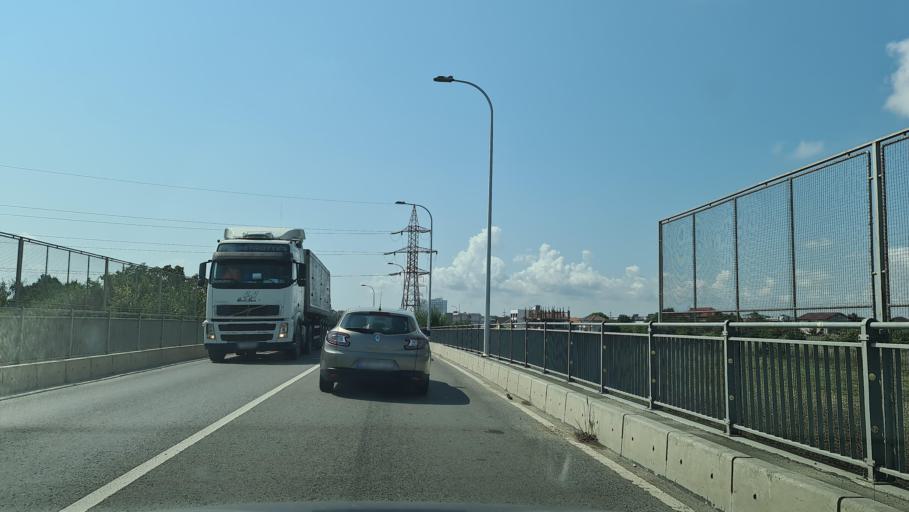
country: RO
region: Constanta
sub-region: Oras Eforie
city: Eforie Nord
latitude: 44.0865
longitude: 28.6399
